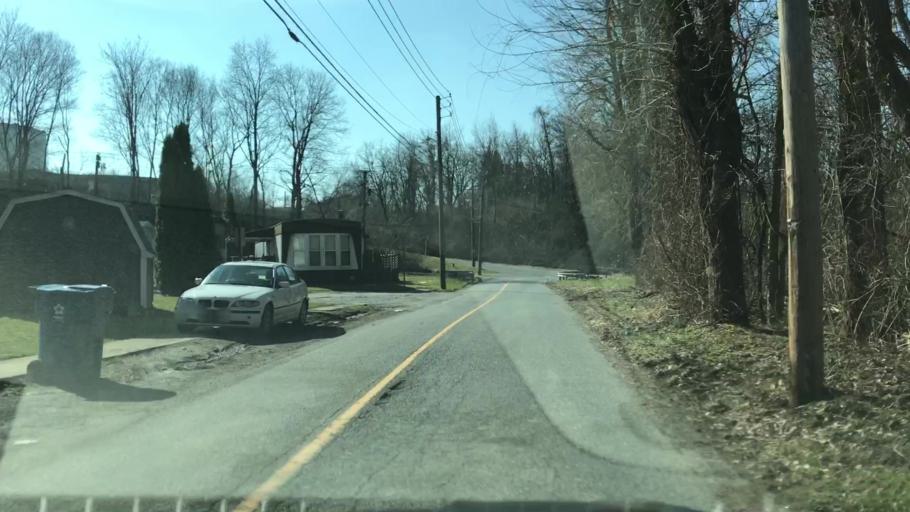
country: US
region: Pennsylvania
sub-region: Dauphin County
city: Highspire
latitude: 40.2212
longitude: -76.7954
